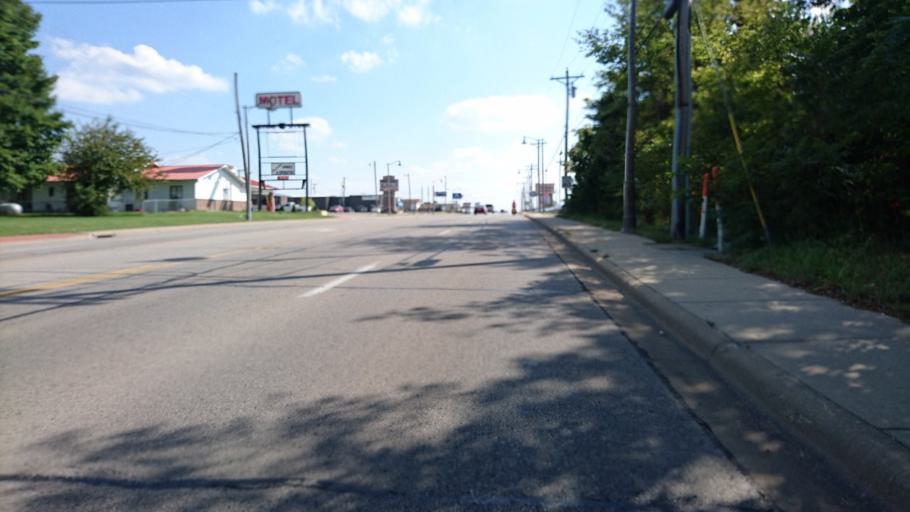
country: US
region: Missouri
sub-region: Laclede County
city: Lebanon
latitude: 37.6547
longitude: -92.6678
